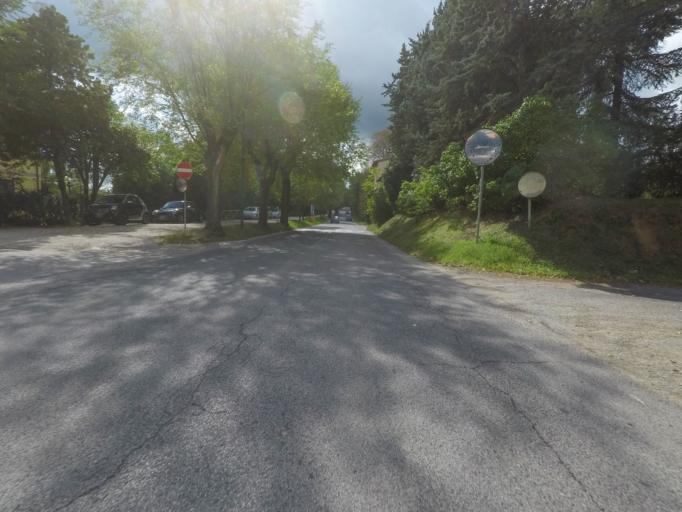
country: IT
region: Tuscany
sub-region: Provincia di Siena
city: Montepulciano
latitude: 43.1045
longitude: 11.7859
